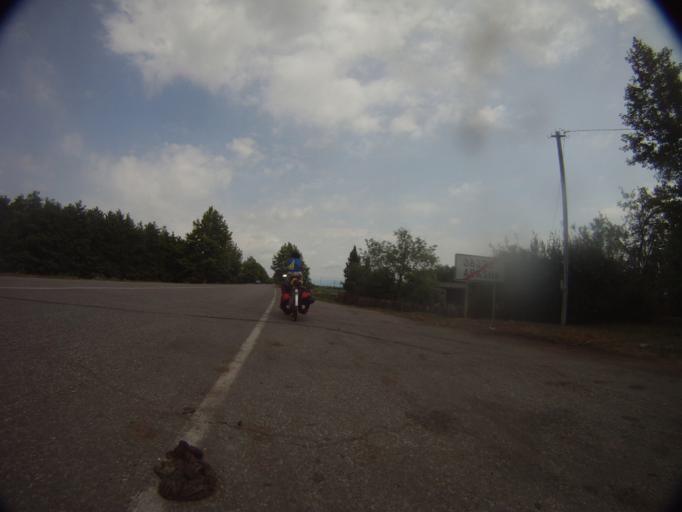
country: GE
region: Samegrelo and Zemo Svaneti
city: Abasha
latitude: 42.2068
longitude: 42.1987
